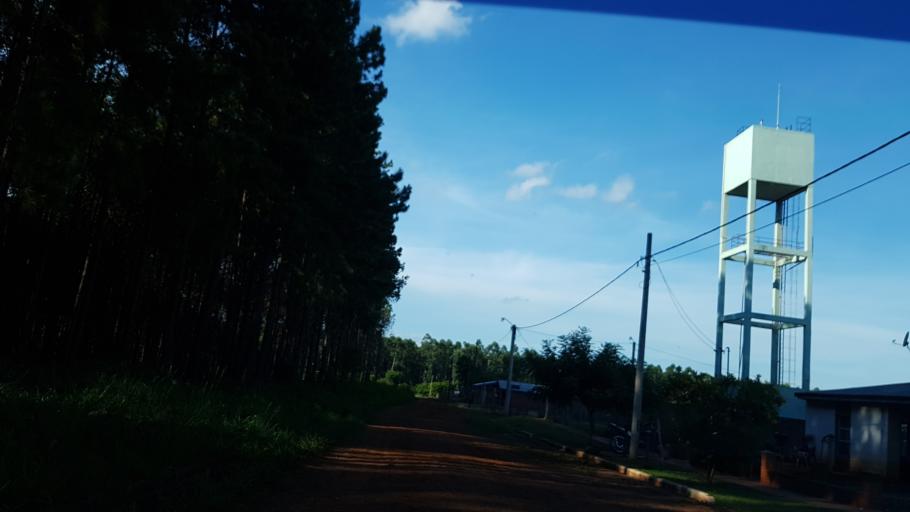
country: AR
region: Misiones
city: Puerto Libertad
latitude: -25.9175
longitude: -54.5907
